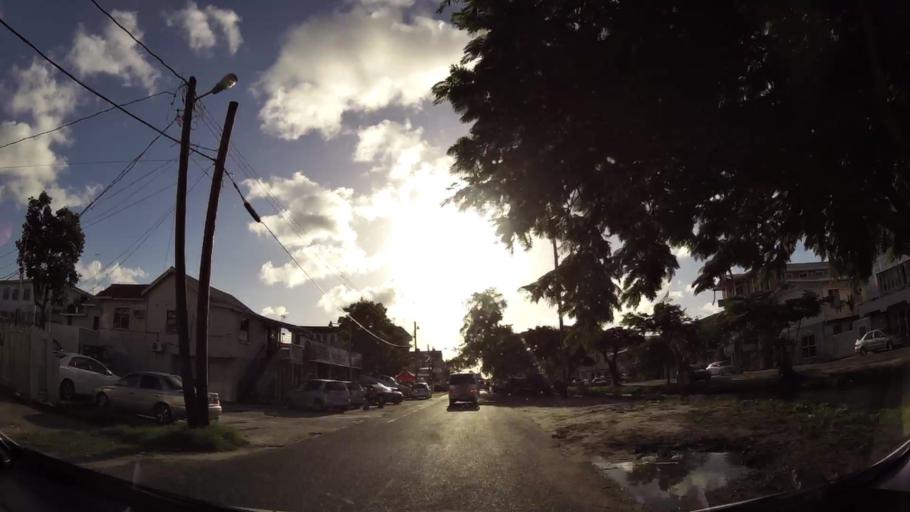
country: GY
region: Demerara-Mahaica
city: Georgetown
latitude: 6.8092
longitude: -58.1638
